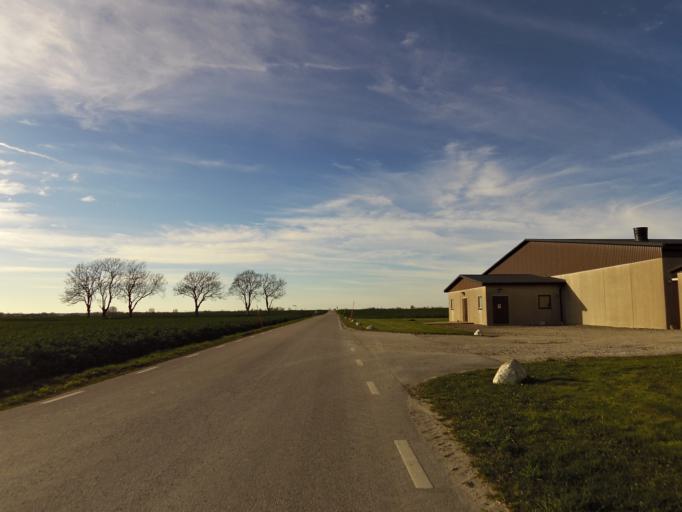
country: SE
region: Skane
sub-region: Kavlinge Kommun
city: Loddekopinge
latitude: 55.7551
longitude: 13.0653
